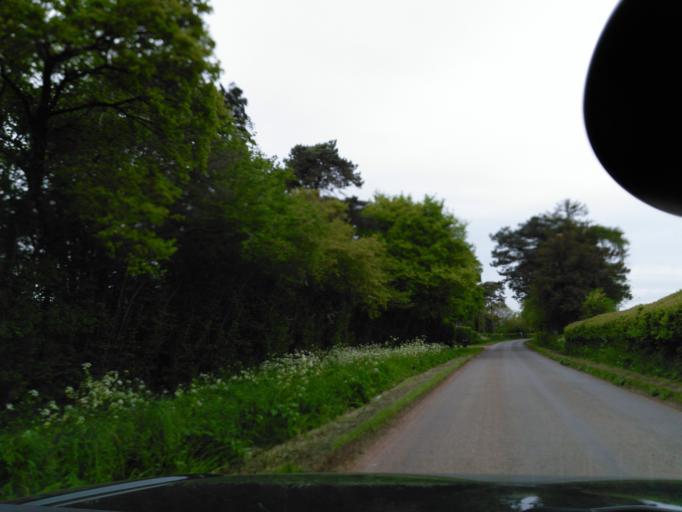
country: GB
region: England
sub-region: Wiltshire
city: Lacock
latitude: 51.4264
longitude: -2.1497
